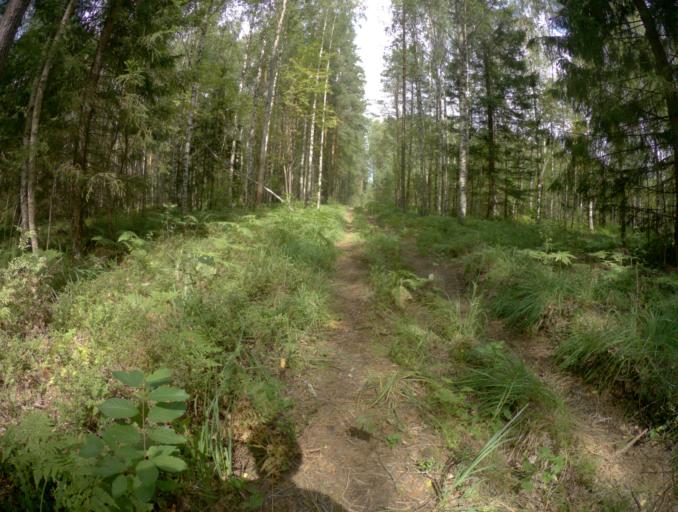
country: RU
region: Vladimir
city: Raduzhnyy
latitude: 55.9640
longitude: 40.2199
